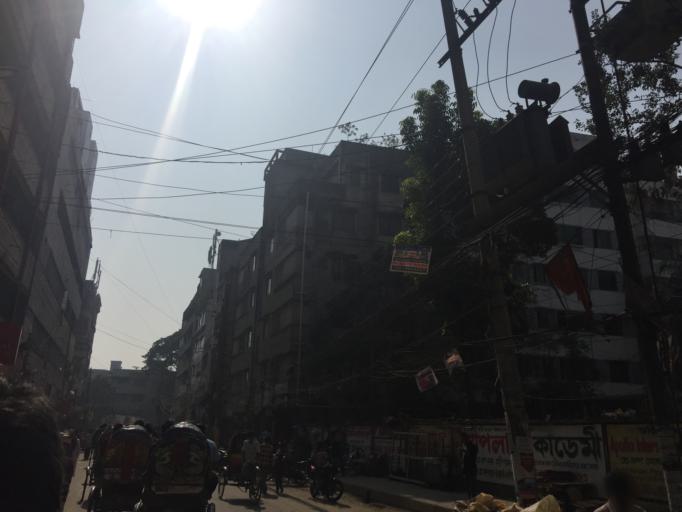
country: BD
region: Dhaka
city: Azimpur
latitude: 23.7393
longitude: 90.3723
